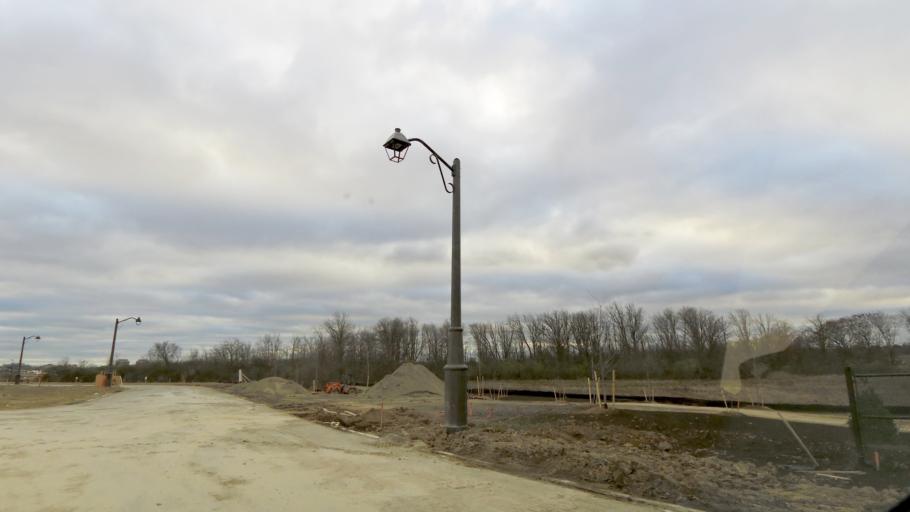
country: CA
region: Ontario
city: Oakville
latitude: 43.4980
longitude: -79.7231
